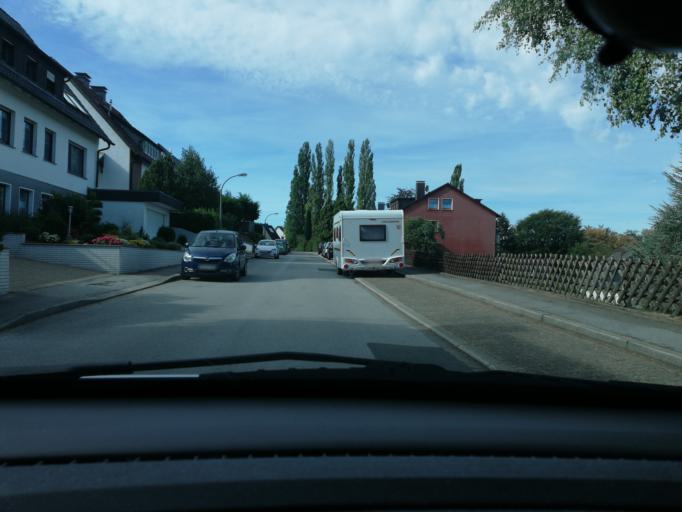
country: DE
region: North Rhine-Westphalia
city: Wetter (Ruhr)
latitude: 51.3759
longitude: 7.3693
